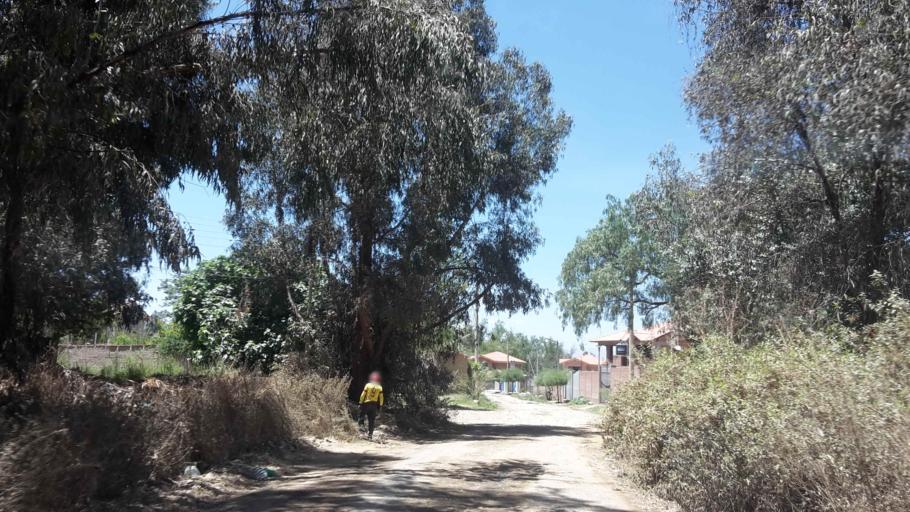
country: BO
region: Cochabamba
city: Cochabamba
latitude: -17.3436
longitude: -66.2155
